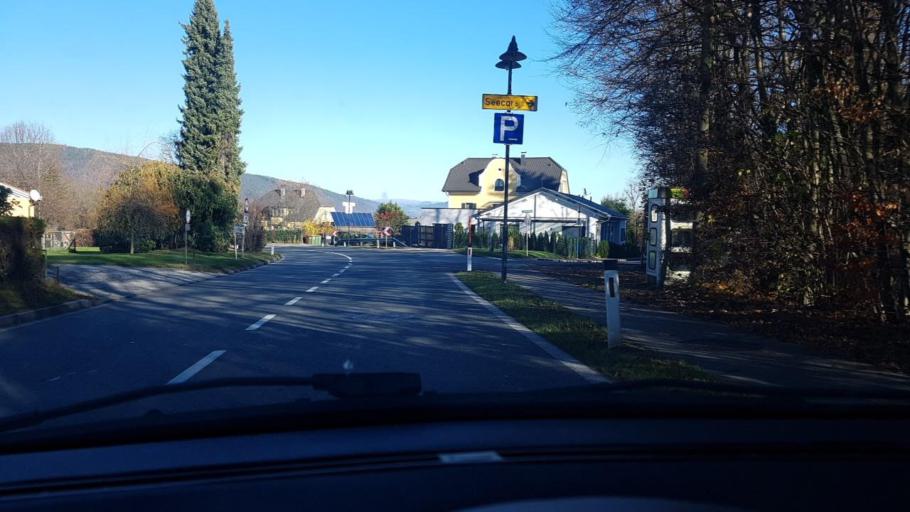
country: AT
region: Carinthia
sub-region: Politischer Bezirk Villach Land
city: Velden am Woerthersee
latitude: 46.6083
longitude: 14.0425
